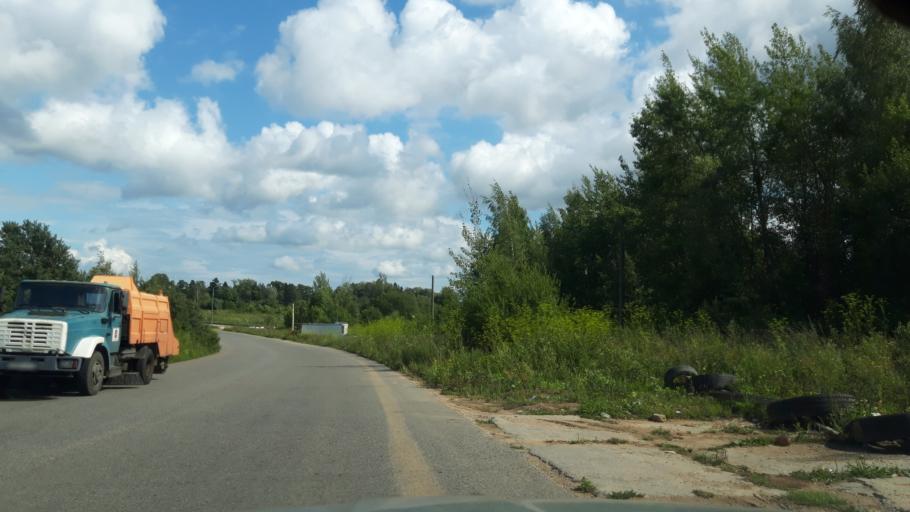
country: RU
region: Moscow
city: Zelenograd
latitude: 55.9642
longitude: 37.1722
